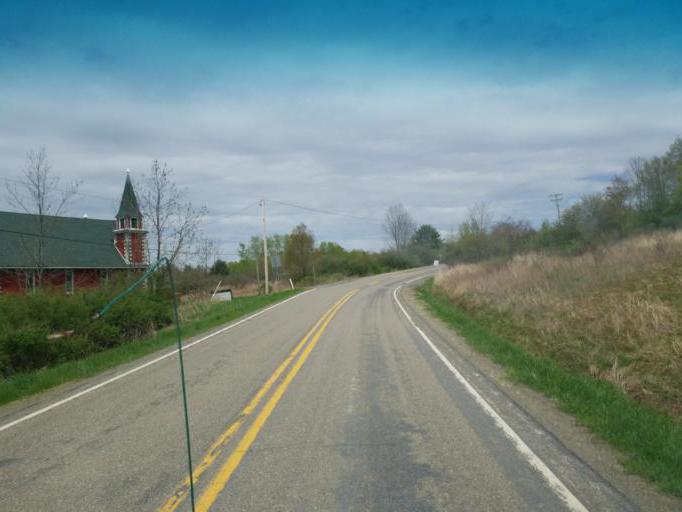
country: US
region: Pennsylvania
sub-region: Tioga County
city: Wellsboro
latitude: 41.6969
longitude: -77.4263
